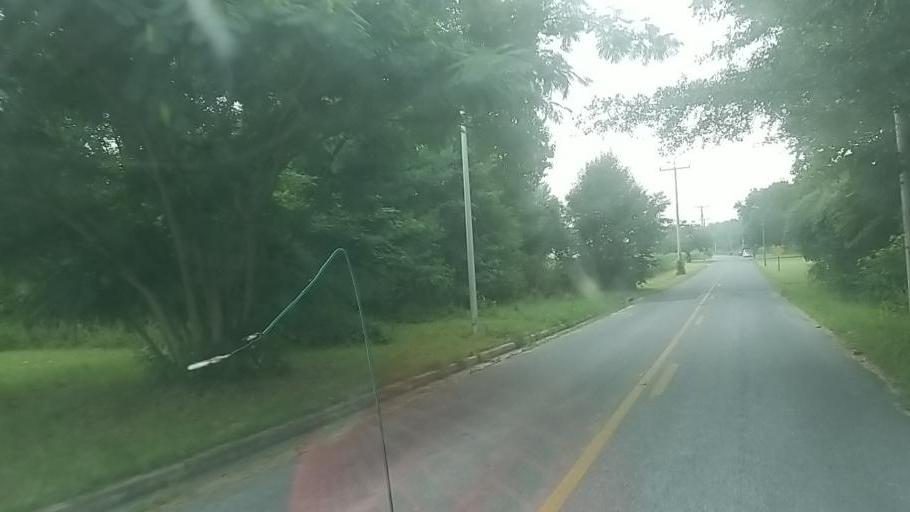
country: US
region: Maryland
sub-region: Wicomico County
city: Salisbury
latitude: 38.3657
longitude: -75.5414
